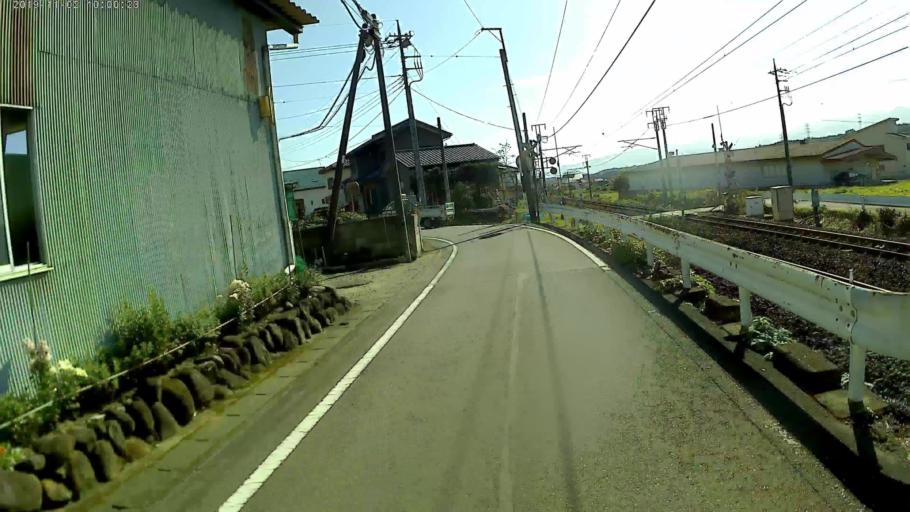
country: JP
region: Gunma
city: Annaka
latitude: 36.3188
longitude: 138.7824
